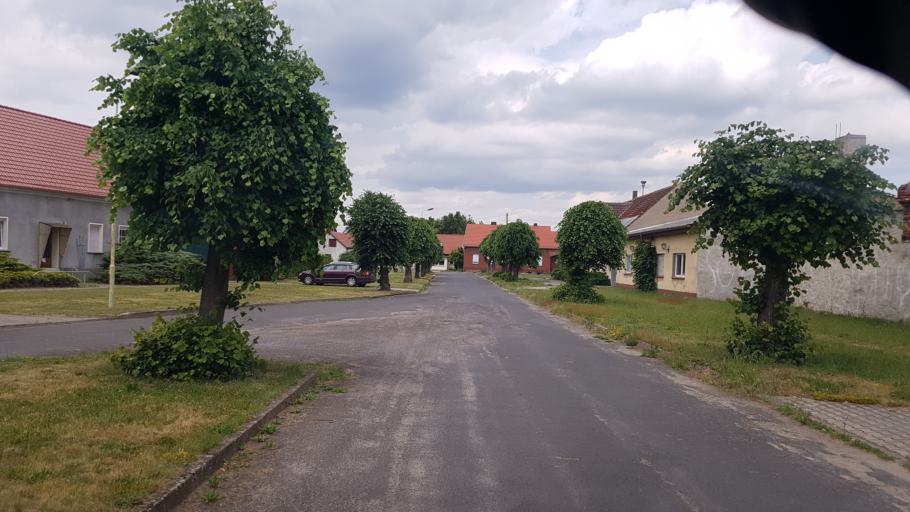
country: DE
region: Brandenburg
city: Ihlow
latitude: 51.8409
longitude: 13.2478
